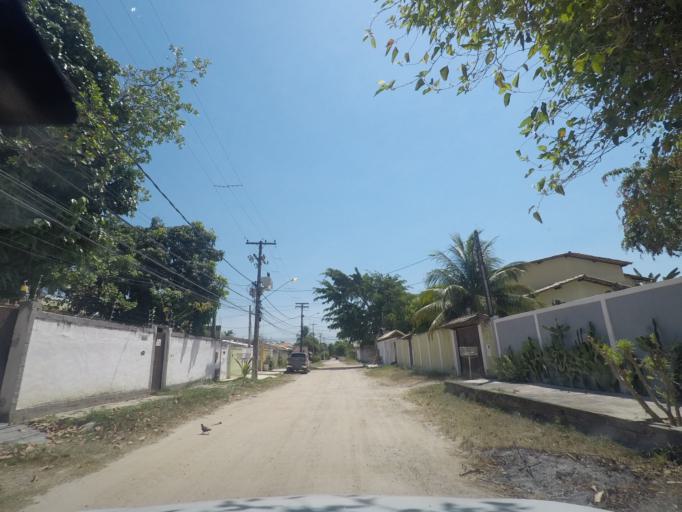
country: BR
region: Rio de Janeiro
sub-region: Niteroi
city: Niteroi
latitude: -22.9352
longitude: -43.0163
